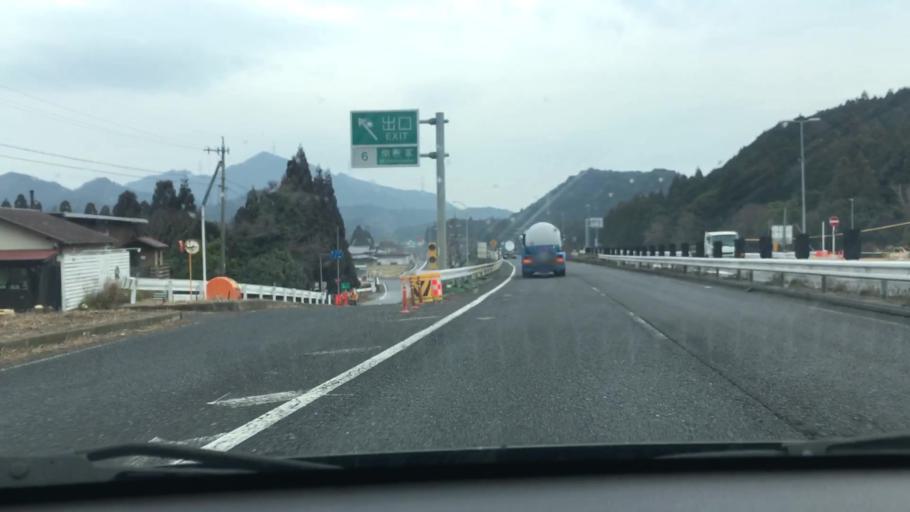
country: JP
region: Mie
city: Kameyama
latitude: 34.8362
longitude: 136.3094
